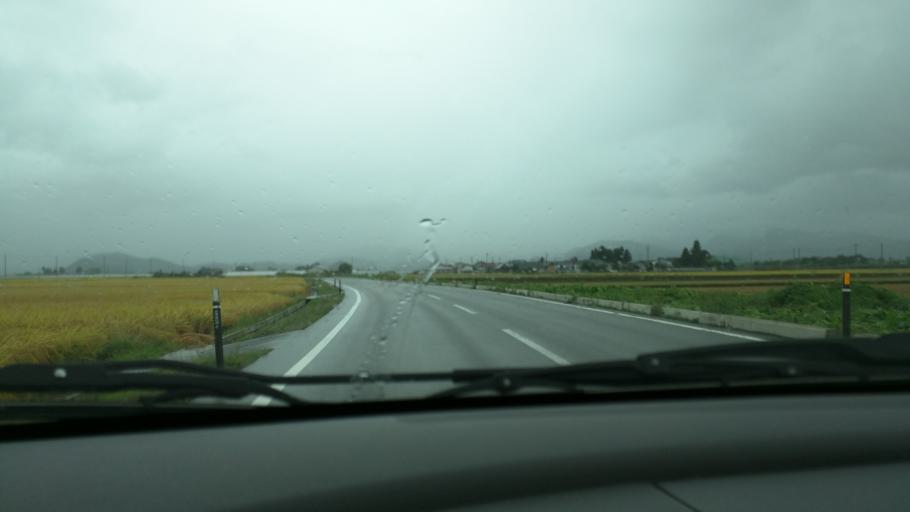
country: JP
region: Fukushima
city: Kitakata
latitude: 37.4846
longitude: 139.8576
